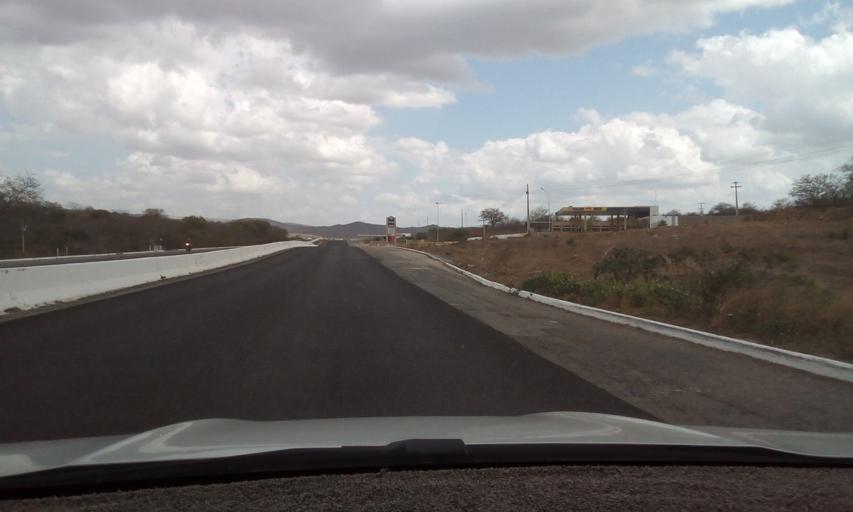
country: BR
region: Pernambuco
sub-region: Toritama
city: Toritama
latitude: -8.0978
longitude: -36.0315
